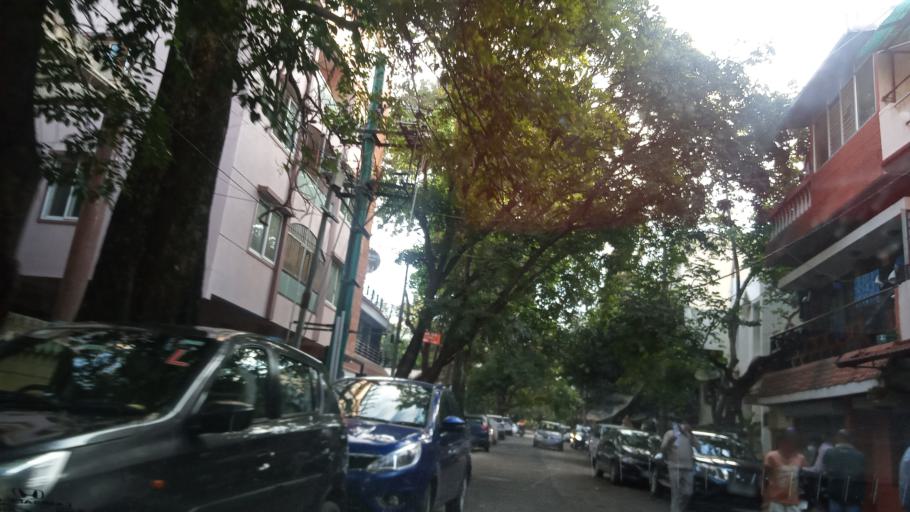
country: IN
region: Karnataka
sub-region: Bangalore Urban
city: Bangalore
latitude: 12.9352
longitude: 77.6203
